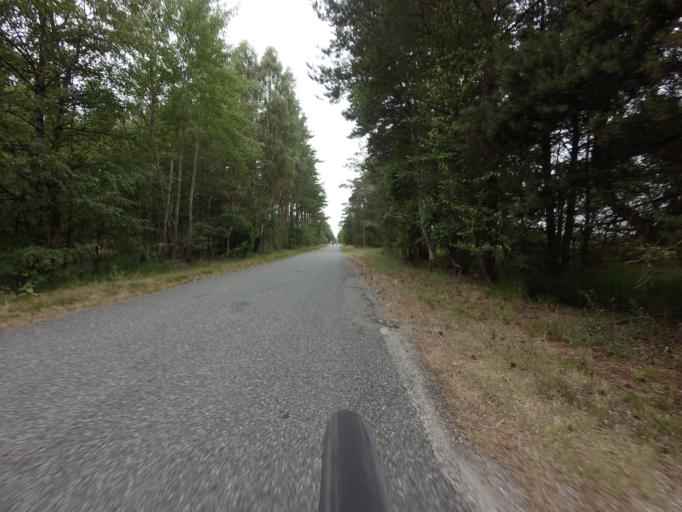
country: DK
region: North Denmark
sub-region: Laeso Kommune
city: Byrum
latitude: 57.2764
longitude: 10.9635
